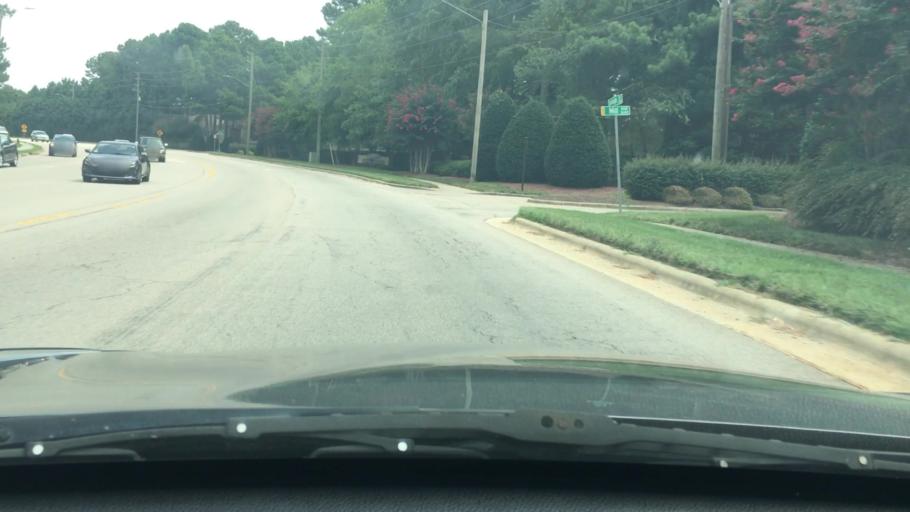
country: US
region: North Carolina
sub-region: Wake County
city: West Raleigh
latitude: 35.8263
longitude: -78.7105
